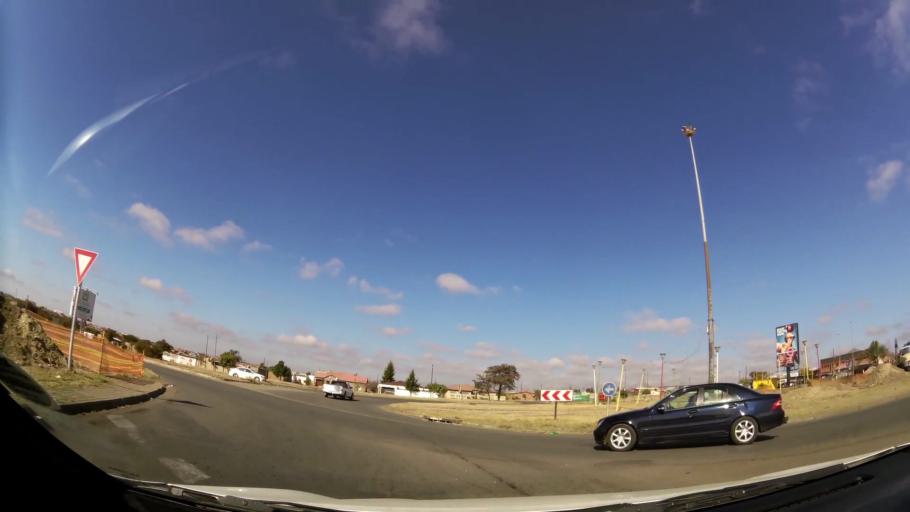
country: ZA
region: Limpopo
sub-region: Capricorn District Municipality
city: Polokwane
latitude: -23.8537
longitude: 29.3988
